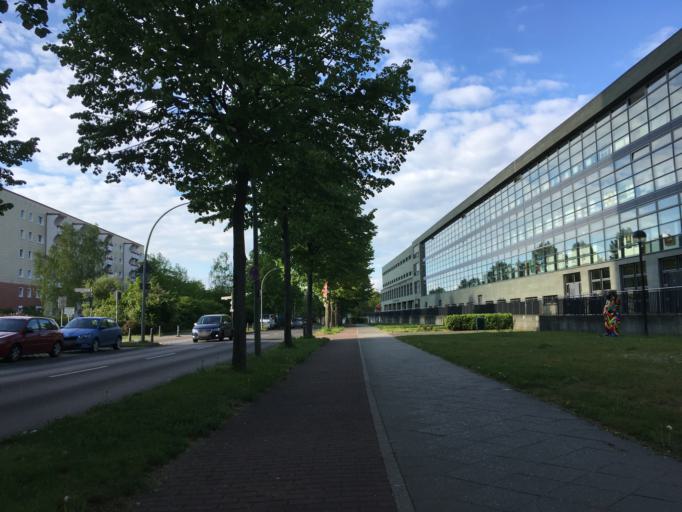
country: DE
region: Berlin
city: Wartenberg
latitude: 52.5698
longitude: 13.5205
